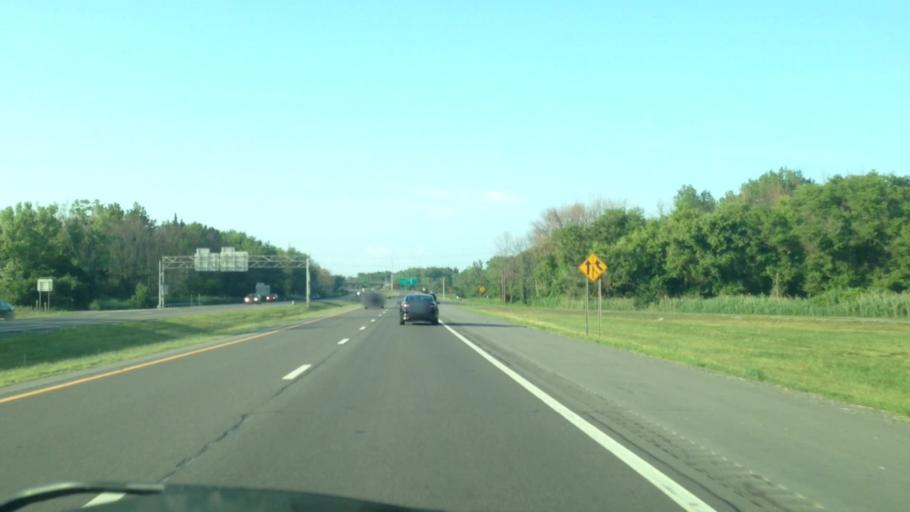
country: US
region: New York
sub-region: Onondaga County
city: East Syracuse
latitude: 43.0357
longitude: -76.0575
